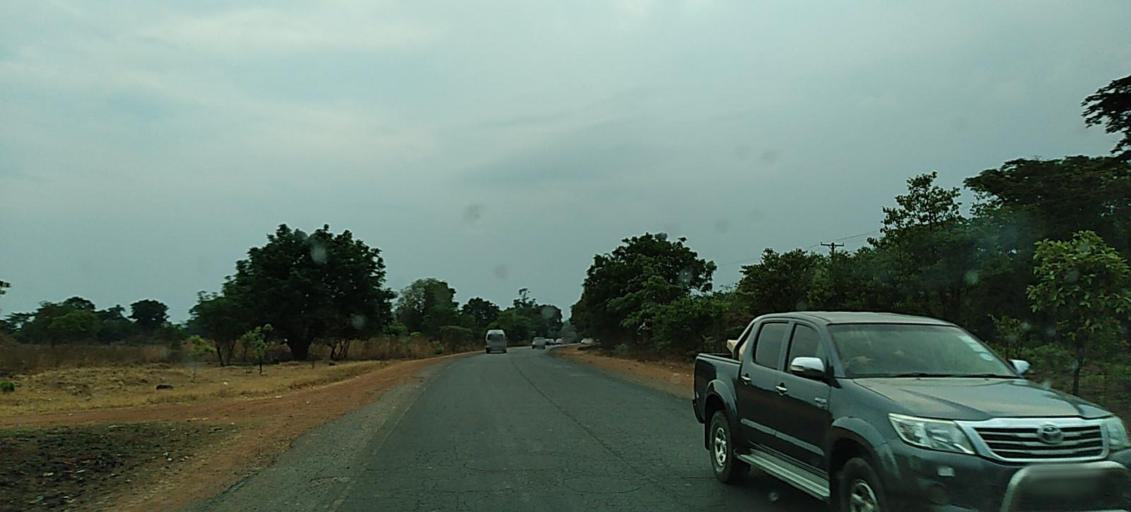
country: ZM
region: Copperbelt
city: Luanshya
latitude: -13.0813
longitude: 28.4448
